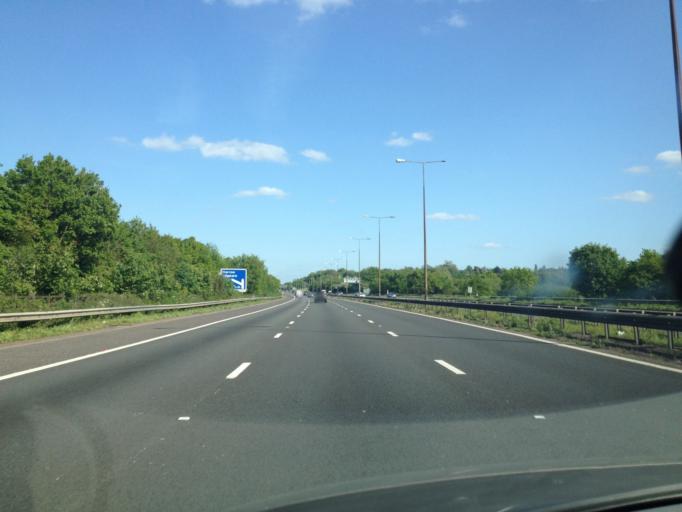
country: GB
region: England
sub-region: Hertfordshire
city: Elstree
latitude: 51.6402
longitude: -0.3172
